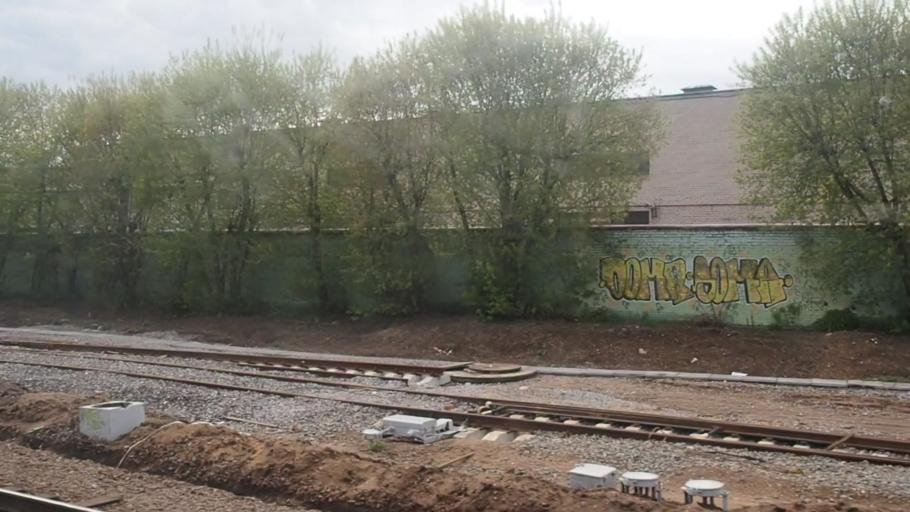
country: RU
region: Moskovskaya
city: Kastanayevo
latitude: 55.7433
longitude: 37.5133
